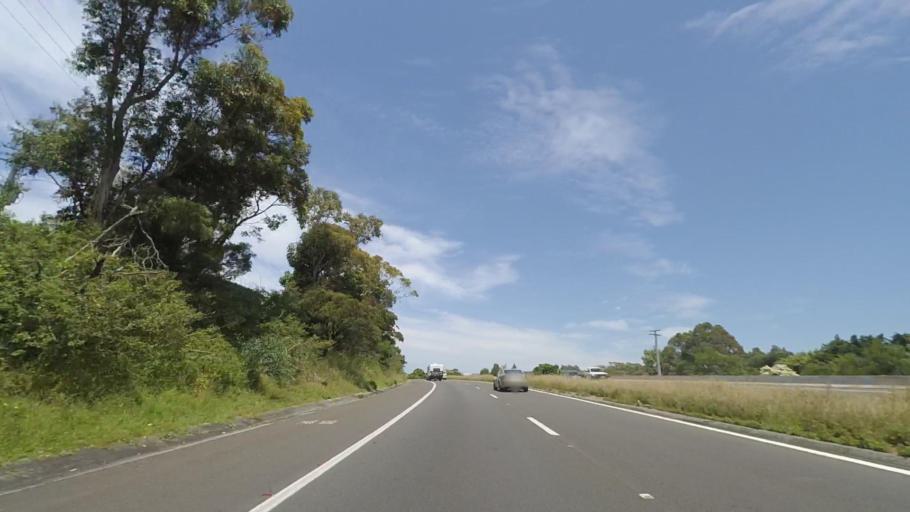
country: AU
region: New South Wales
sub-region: Kiama
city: Kiama
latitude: -34.6727
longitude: 150.8429
